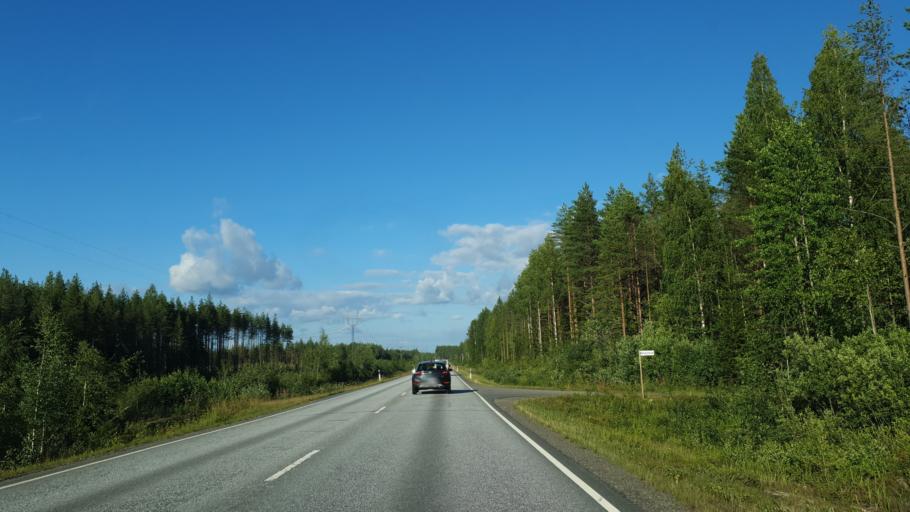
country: FI
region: North Karelia
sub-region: Joensuu
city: Outokumpu
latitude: 62.5312
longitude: 29.0888
